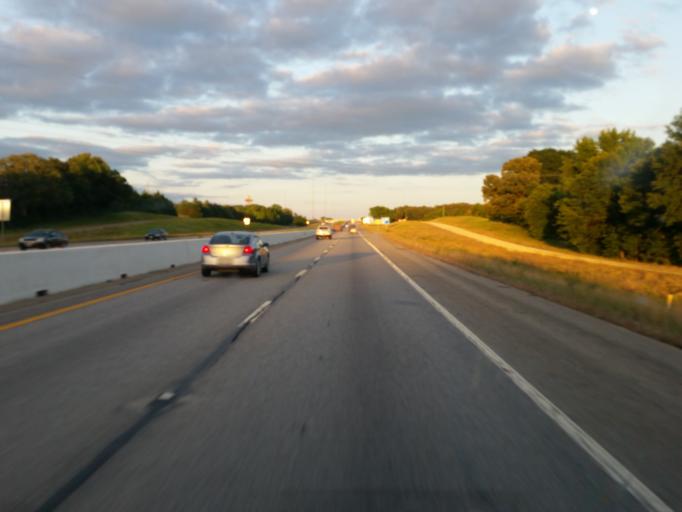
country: US
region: Texas
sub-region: Van Zandt County
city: Van
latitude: 32.5090
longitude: -95.6567
